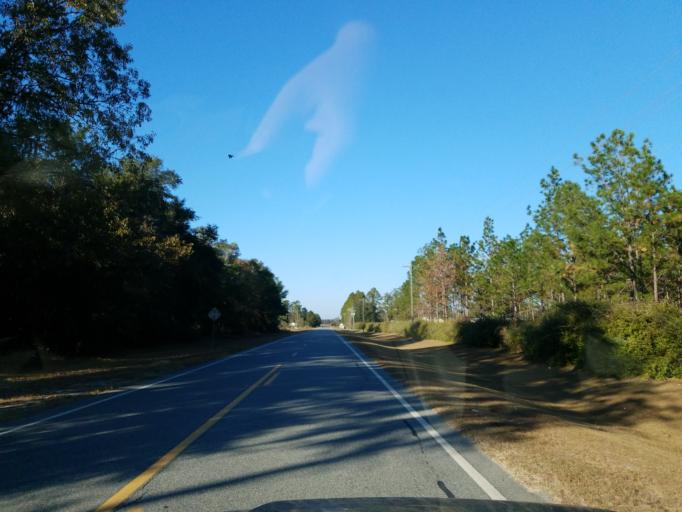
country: US
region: Georgia
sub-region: Echols County
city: Statenville
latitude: 30.6635
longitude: -83.0610
